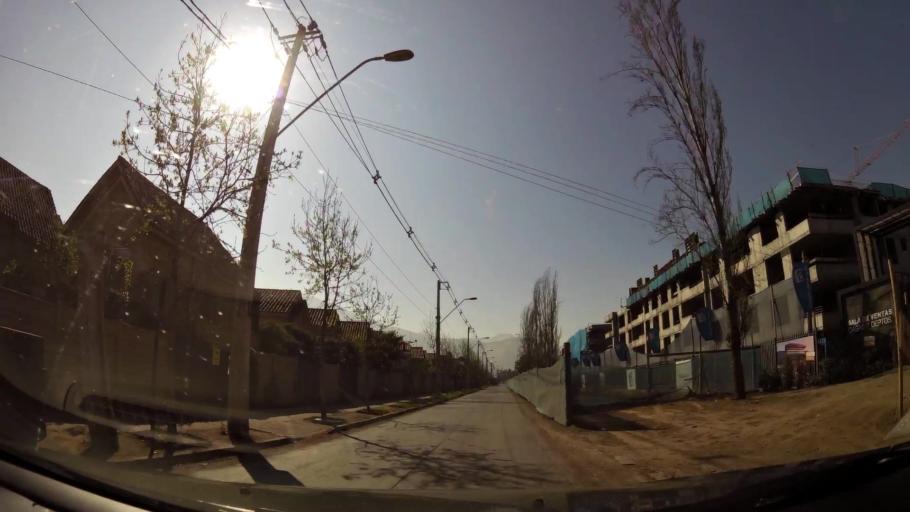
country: CL
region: Santiago Metropolitan
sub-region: Provincia de Chacabuco
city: Chicureo Abajo
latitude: -33.3541
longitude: -70.6835
